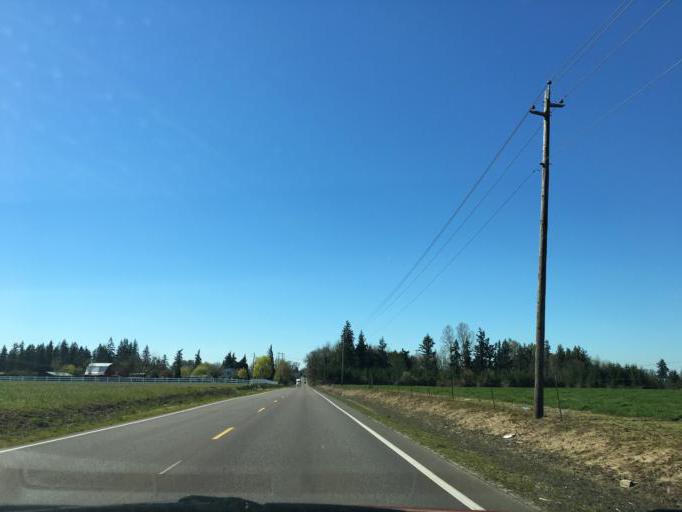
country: US
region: Oregon
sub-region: Marion County
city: Hubbard
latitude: 45.1442
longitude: -122.7395
